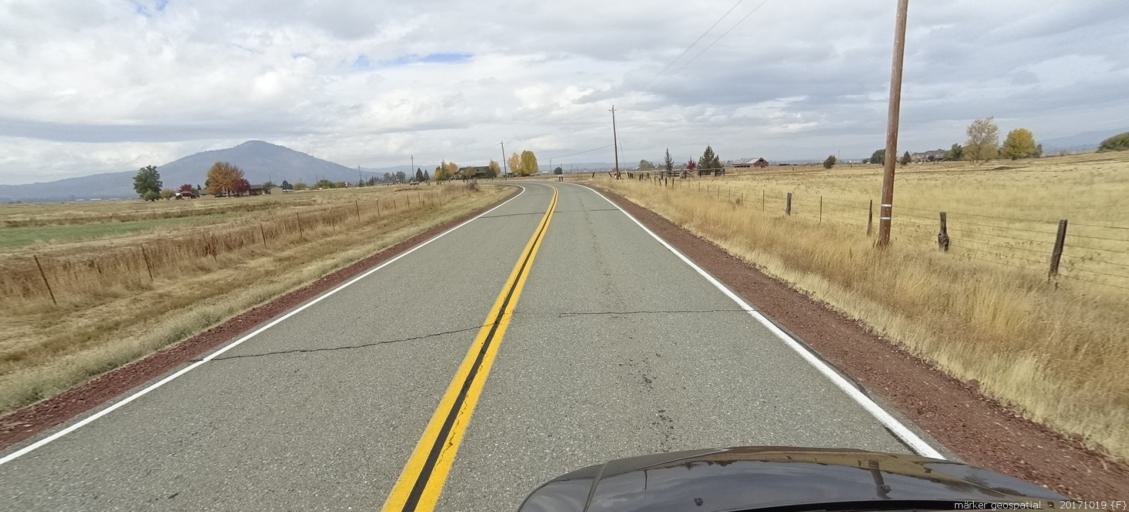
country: US
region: California
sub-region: Shasta County
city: Burney
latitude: 41.0609
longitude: -121.4650
